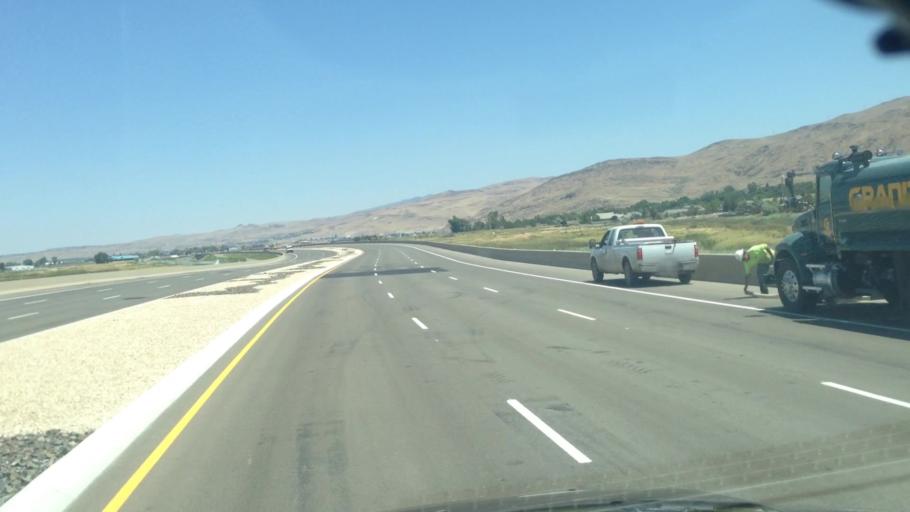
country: US
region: Nevada
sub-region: Washoe County
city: Sparks
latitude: 39.4881
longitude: -119.7347
